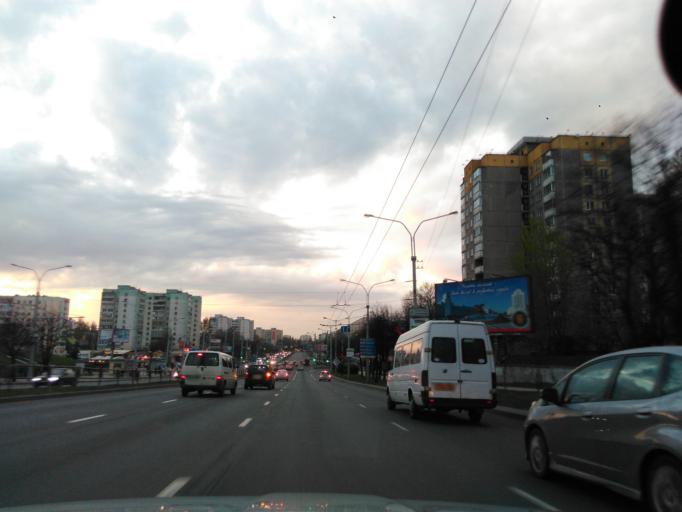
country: BY
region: Minsk
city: Novoye Medvezhino
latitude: 53.9072
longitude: 27.4961
